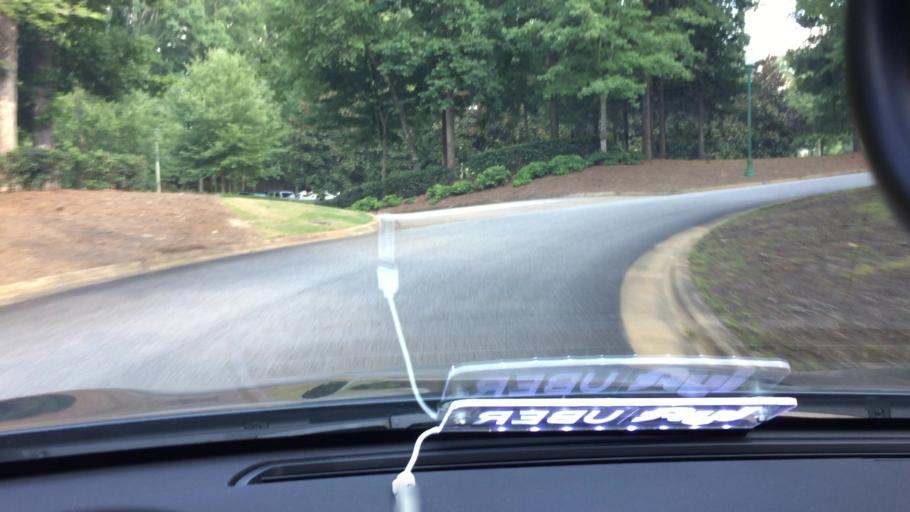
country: US
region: Alabama
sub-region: Lee County
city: Auburn
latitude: 32.5810
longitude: -85.4456
